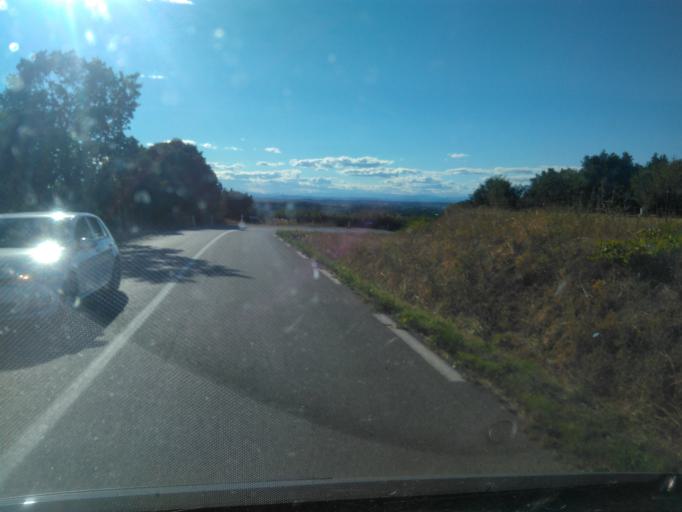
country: FR
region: Languedoc-Roussillon
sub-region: Departement du Gard
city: Vauvert
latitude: 43.6807
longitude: 4.2773
